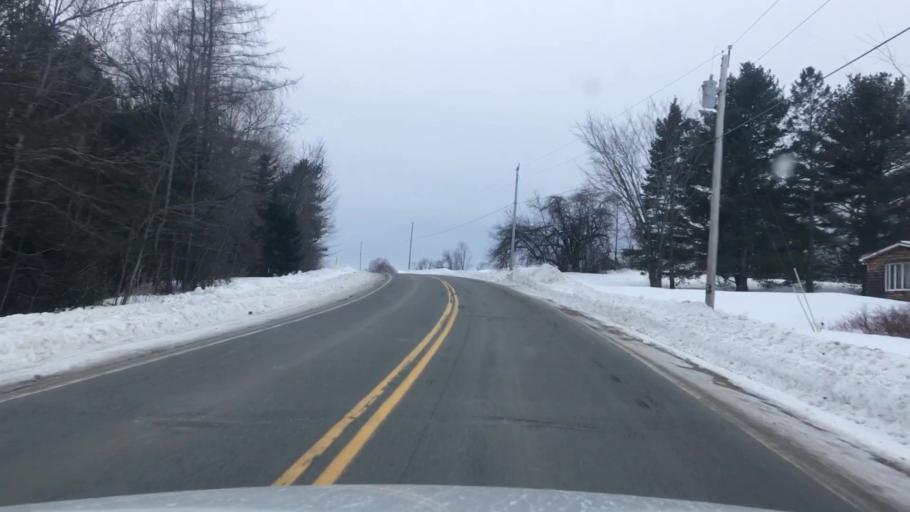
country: US
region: Maine
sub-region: Penobscot County
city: Corinna
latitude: 44.9515
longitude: -69.2039
